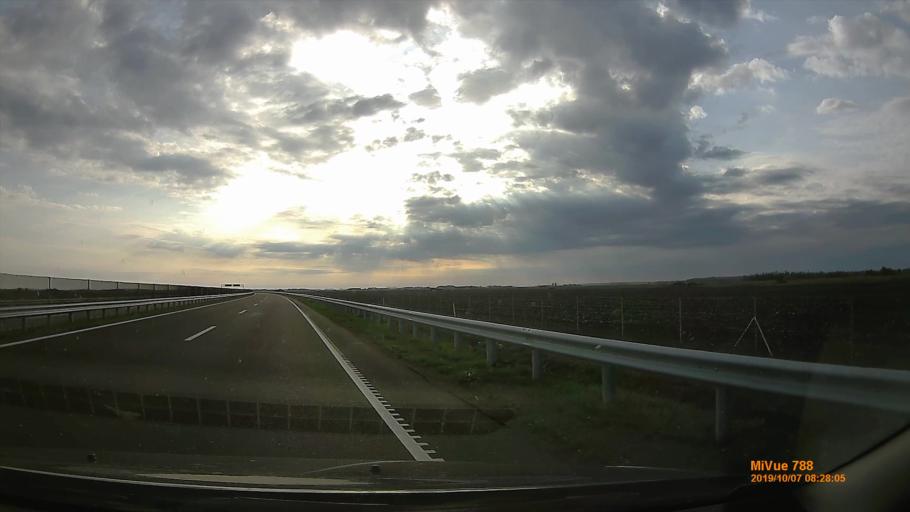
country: HU
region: Jasz-Nagykun-Szolnok
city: Ocsod
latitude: 46.8127
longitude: 20.3934
